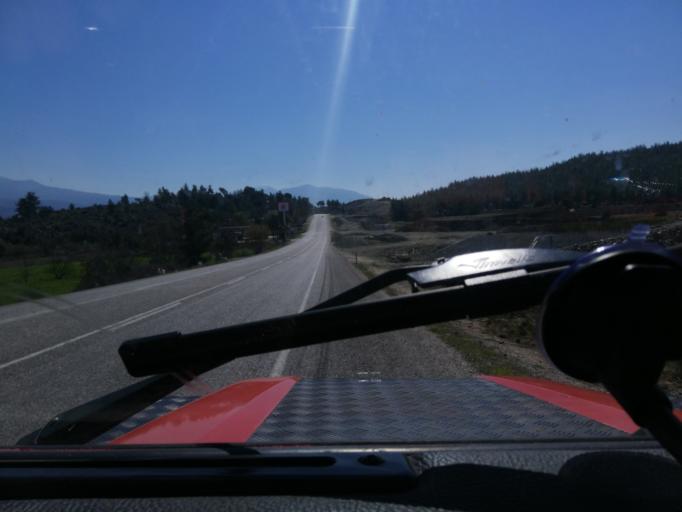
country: TR
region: Mugla
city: Kemer
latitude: 36.6152
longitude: 29.3573
